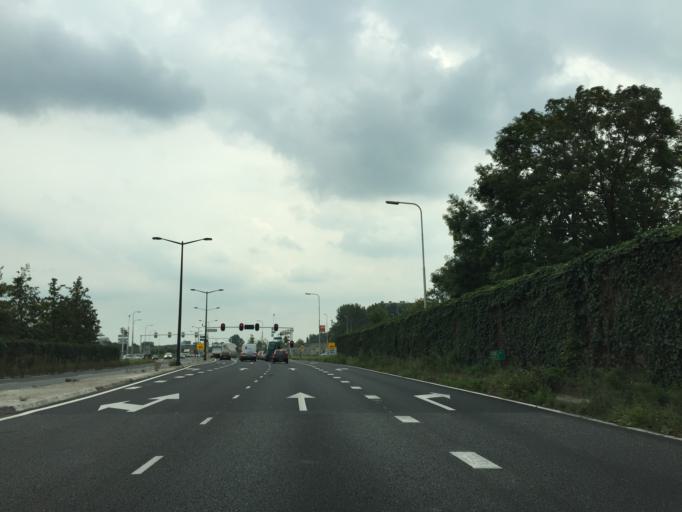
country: NL
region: South Holland
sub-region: Gemeente Leidschendam-Voorburg
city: Voorburg
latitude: 52.1026
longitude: 4.3621
